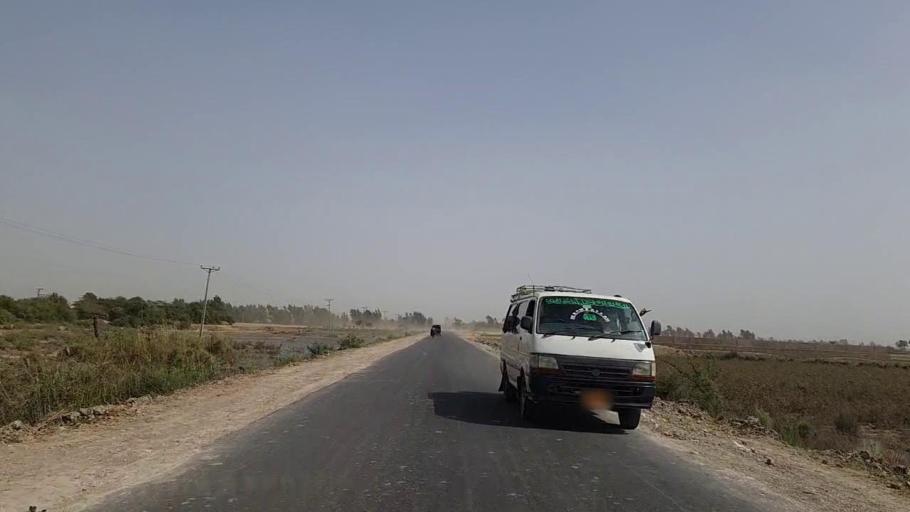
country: PK
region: Sindh
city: Tando Bago
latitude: 24.7961
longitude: 68.9493
